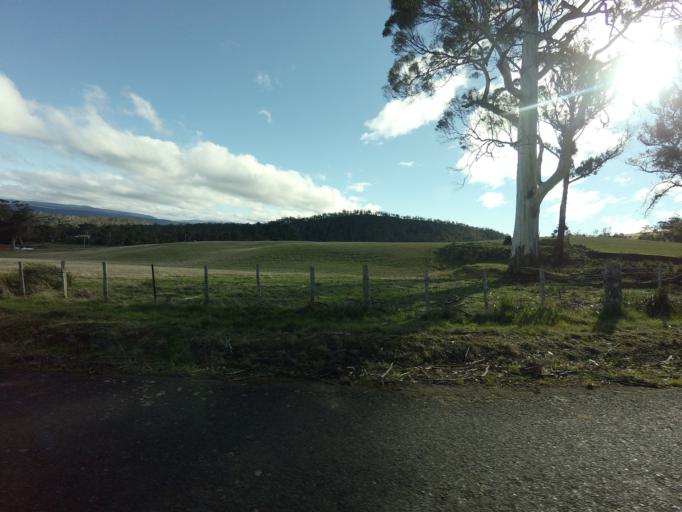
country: AU
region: Tasmania
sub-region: Derwent Valley
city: New Norfolk
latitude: -42.7237
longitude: 147.0327
